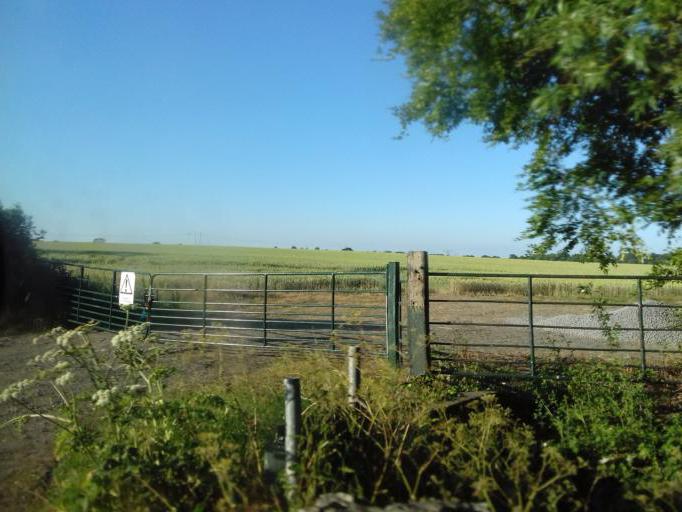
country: IE
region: Leinster
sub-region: Fingal County
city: Blanchardstown
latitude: 53.4513
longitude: -6.3392
